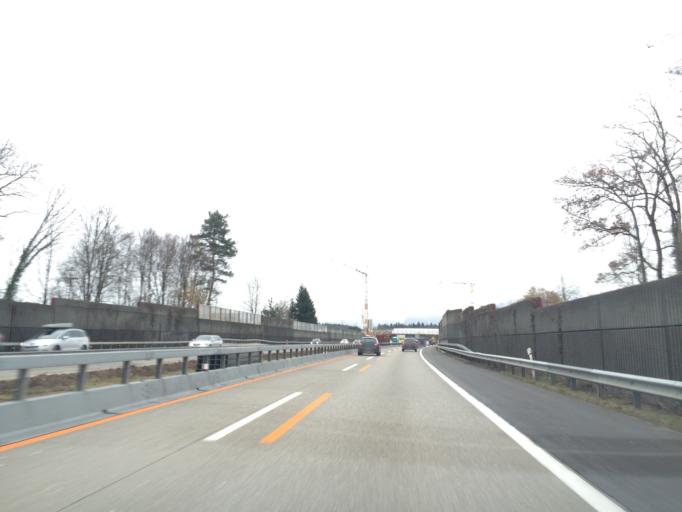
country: CH
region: Bern
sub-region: Thun District
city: Uttigen
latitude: 46.8197
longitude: 7.5731
